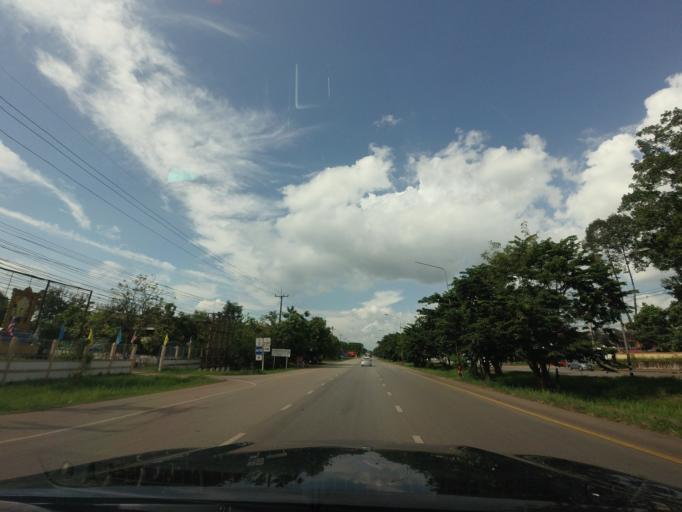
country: TH
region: Nong Khai
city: Sa Khrai
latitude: 17.5524
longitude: 102.8008
